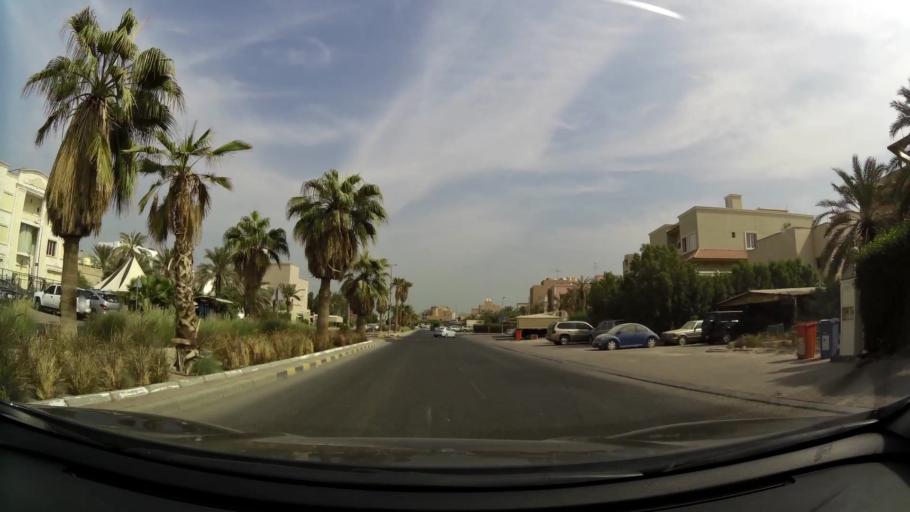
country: KW
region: Al Asimah
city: Ash Shamiyah
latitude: 29.3359
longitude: 47.9742
